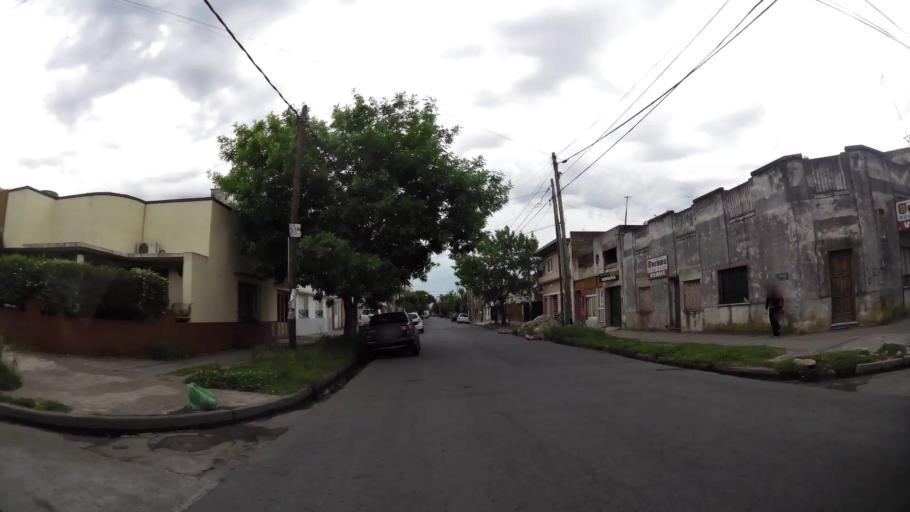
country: AR
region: Buenos Aires
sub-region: Partido de Lanus
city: Lanus
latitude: -34.6867
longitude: -58.3898
